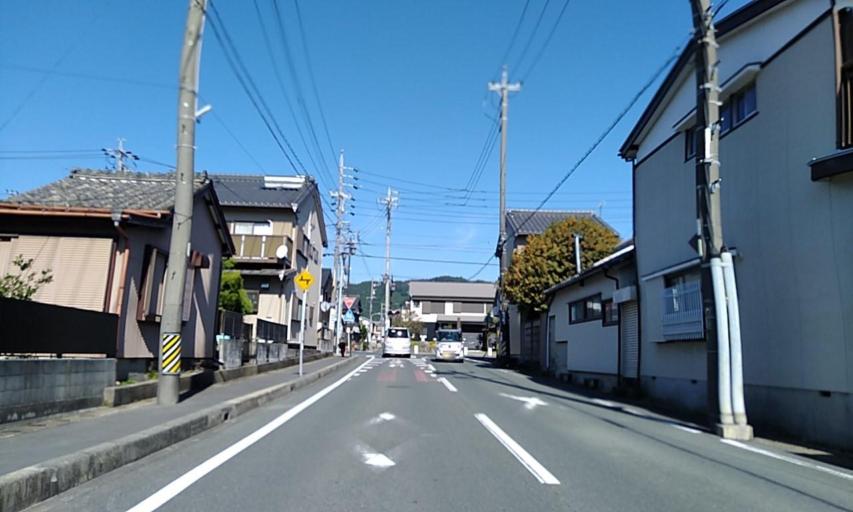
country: JP
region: Shizuoka
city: Kosai-shi
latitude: 34.7229
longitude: 137.4516
